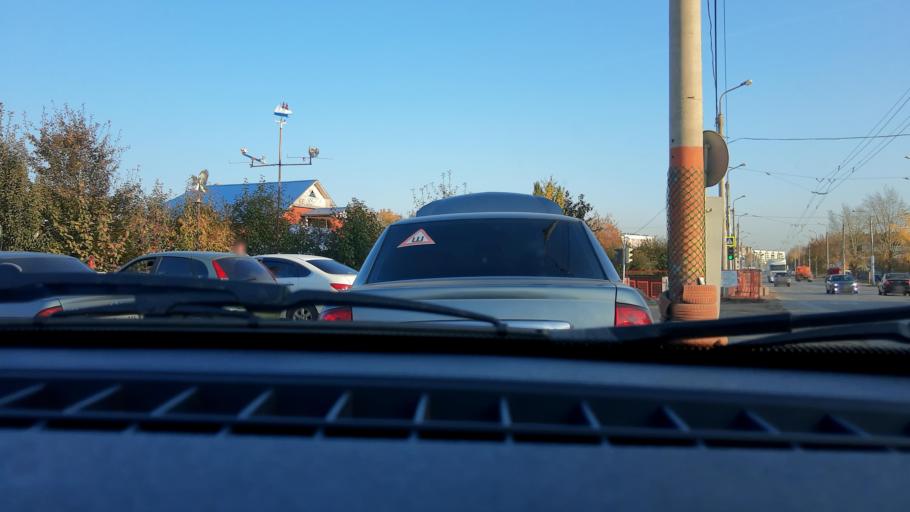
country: RU
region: Bashkortostan
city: Mikhaylovka
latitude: 54.7938
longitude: 55.8749
